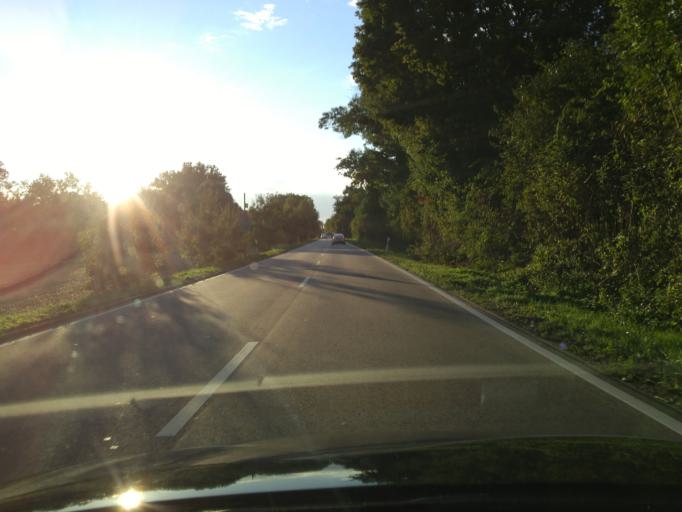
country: DE
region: Baden-Wuerttemberg
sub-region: Regierungsbezirk Stuttgart
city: Untereisesheim
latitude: 49.1870
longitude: 9.1903
